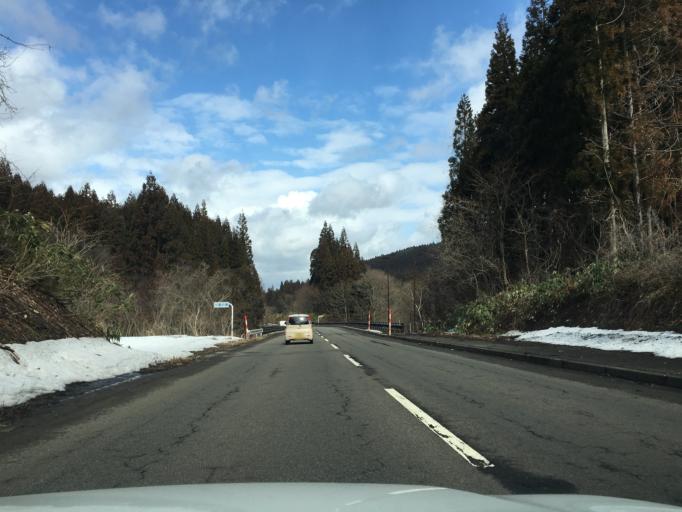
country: JP
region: Akita
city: Takanosu
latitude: 40.0116
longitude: 140.2788
